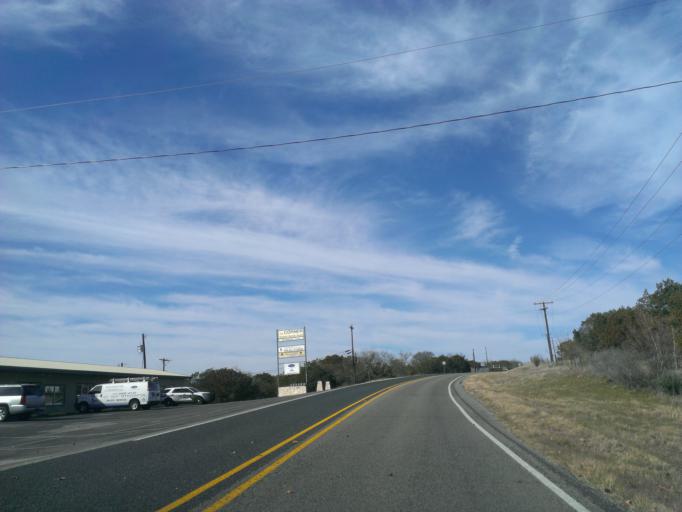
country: US
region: Texas
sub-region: Burnet County
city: Granite Shoals
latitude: 30.5942
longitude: -98.4266
